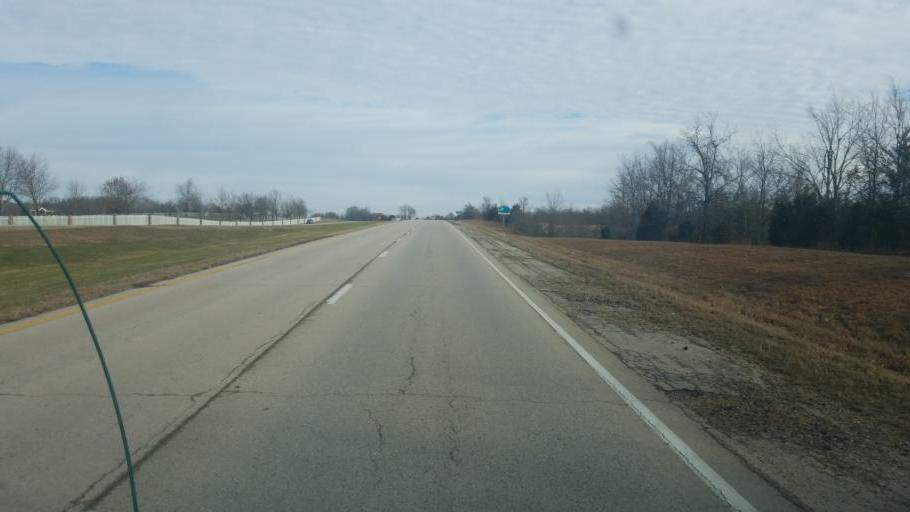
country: US
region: Missouri
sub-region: Stoddard County
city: Bloomfield
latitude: 36.8611
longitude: -89.9336
